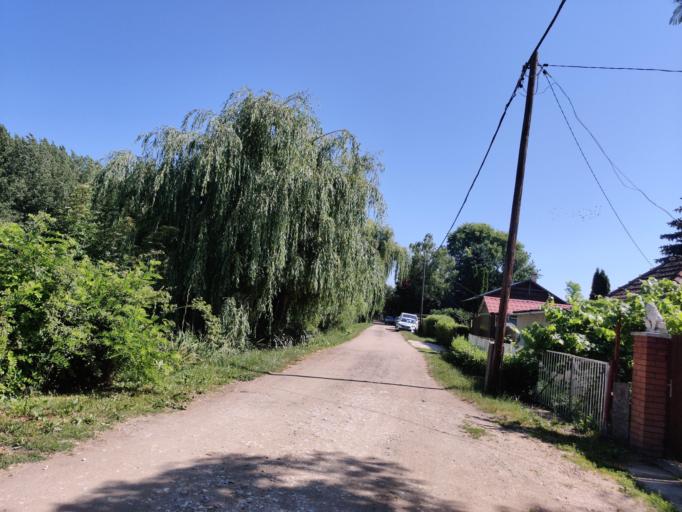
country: HU
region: Hajdu-Bihar
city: Balmazujvaros
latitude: 47.5916
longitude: 21.3692
